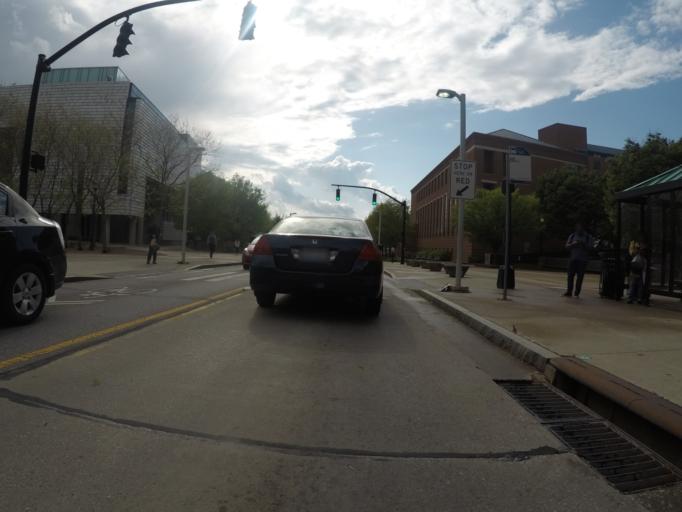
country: US
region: Ohio
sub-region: Franklin County
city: Grandview Heights
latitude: 40.0041
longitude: -83.0155
